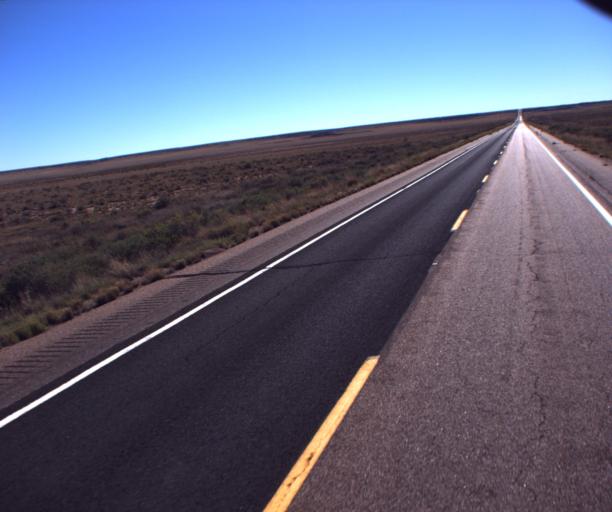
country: US
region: Arizona
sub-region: Navajo County
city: Snowflake
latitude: 34.7403
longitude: -109.7917
